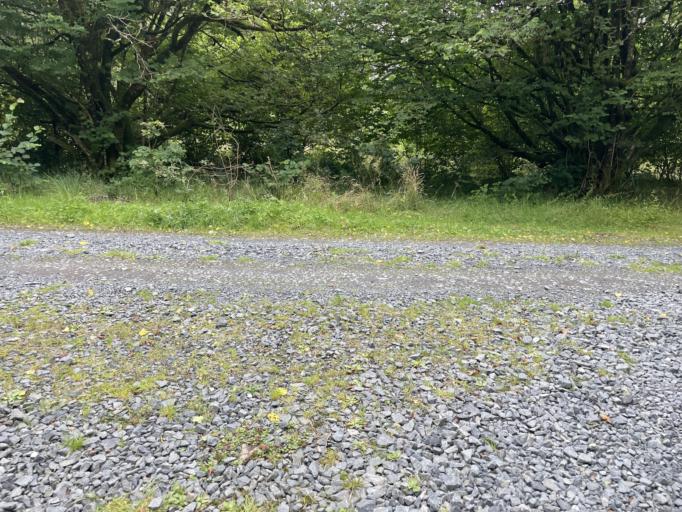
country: GB
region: Scotland
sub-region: Dumfries and Galloway
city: Newton Stewart
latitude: 55.0790
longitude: -4.5094
